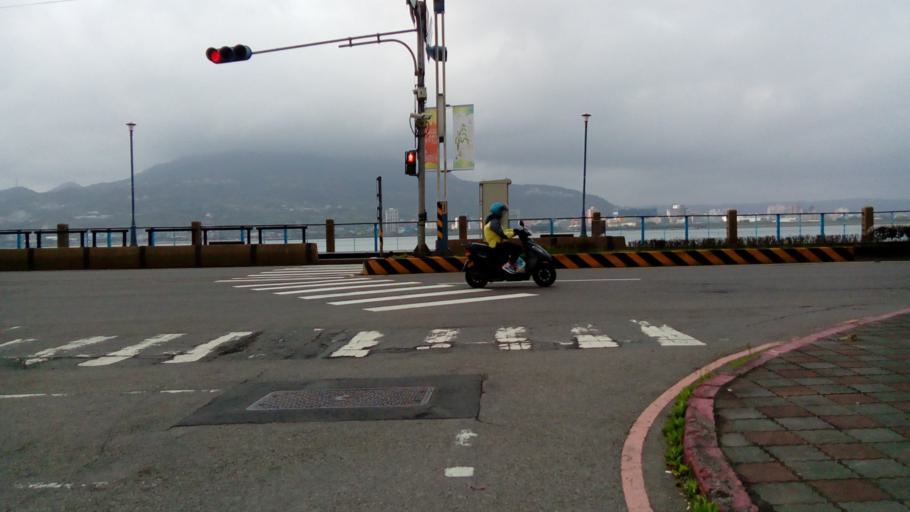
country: TW
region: Taipei
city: Taipei
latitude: 25.1758
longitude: 121.4282
